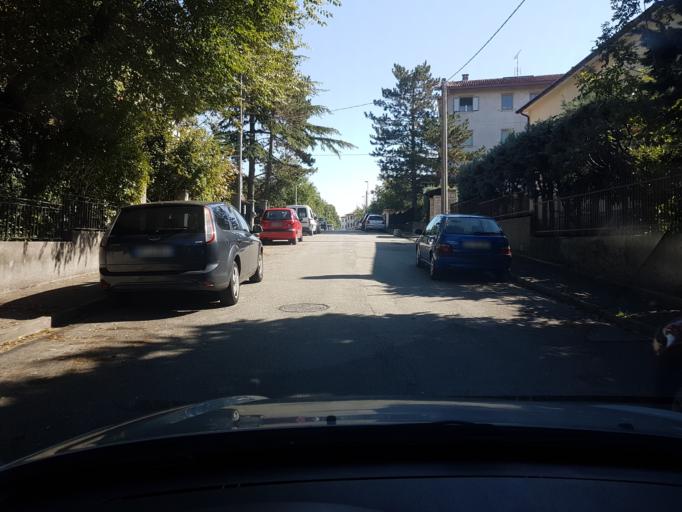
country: IT
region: Friuli Venezia Giulia
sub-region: Provincia di Trieste
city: Aurisina Cave
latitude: 45.7530
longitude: 13.6596
